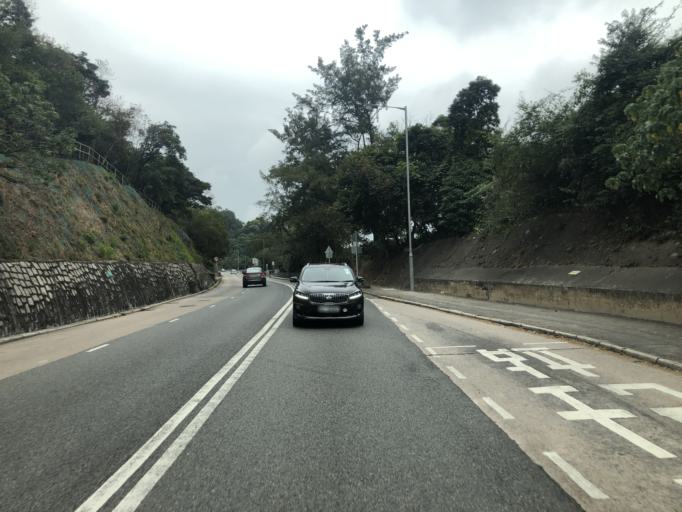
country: HK
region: Wong Tai Sin
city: Wong Tai Sin
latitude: 22.3339
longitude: 114.2214
